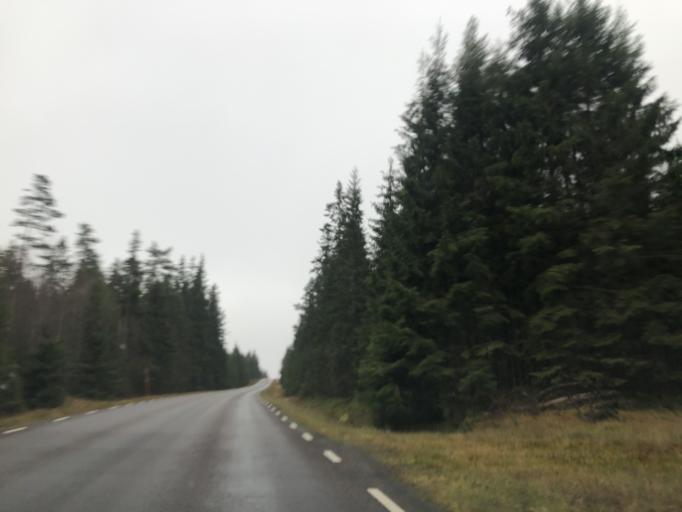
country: SE
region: Vaestra Goetaland
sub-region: Ulricehamns Kommun
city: Ulricehamn
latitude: 57.7393
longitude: 13.5395
